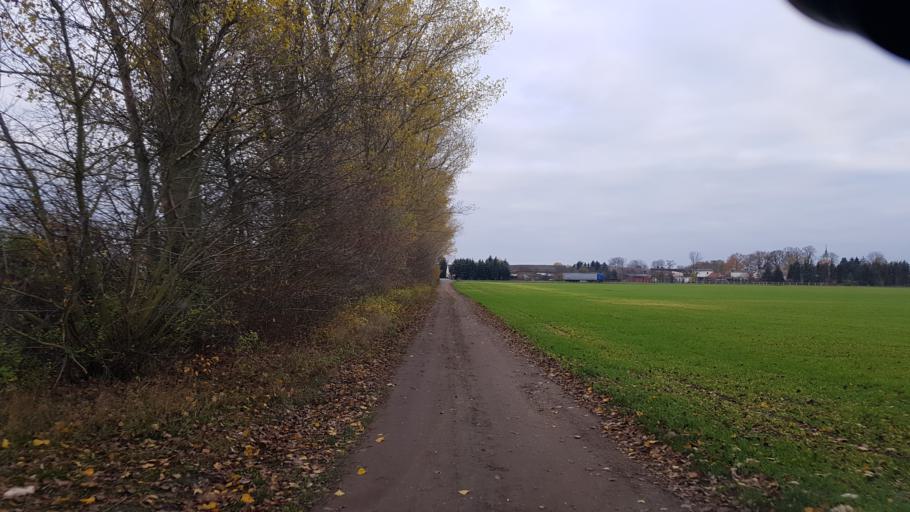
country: DE
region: Brandenburg
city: Sallgast
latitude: 51.6097
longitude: 13.8679
